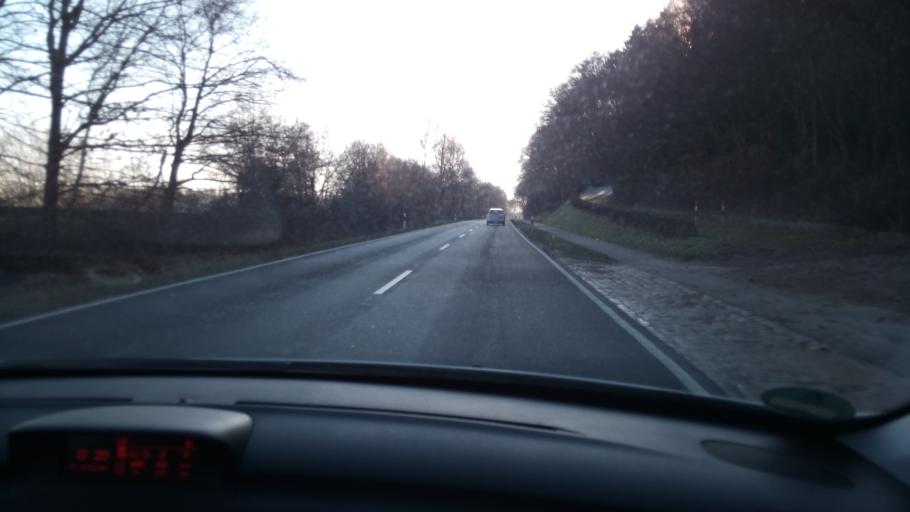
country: DE
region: Schleswig-Holstein
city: Buchen
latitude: 53.4668
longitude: 10.6238
